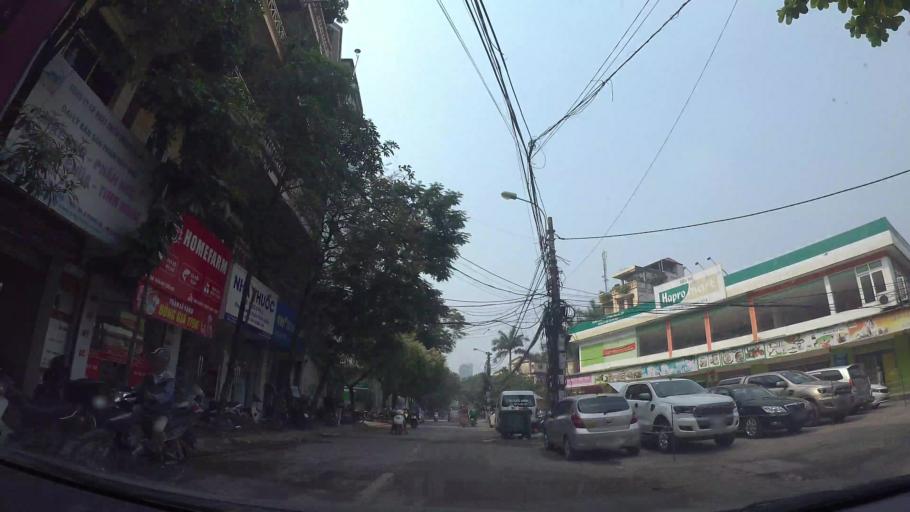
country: VN
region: Ha Noi
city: Dong Da
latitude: 21.0229
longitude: 105.8162
